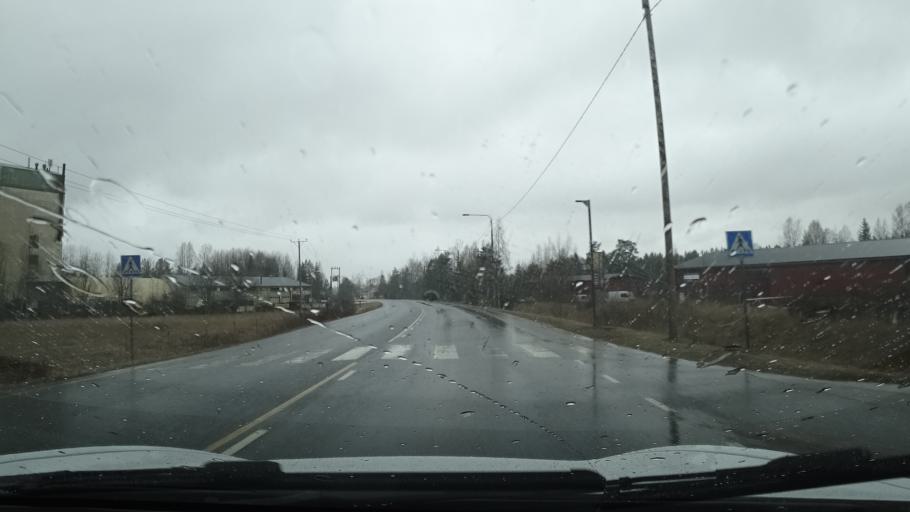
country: FI
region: Paijanne Tavastia
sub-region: Lahti
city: Orimattila
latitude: 60.8019
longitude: 25.7691
